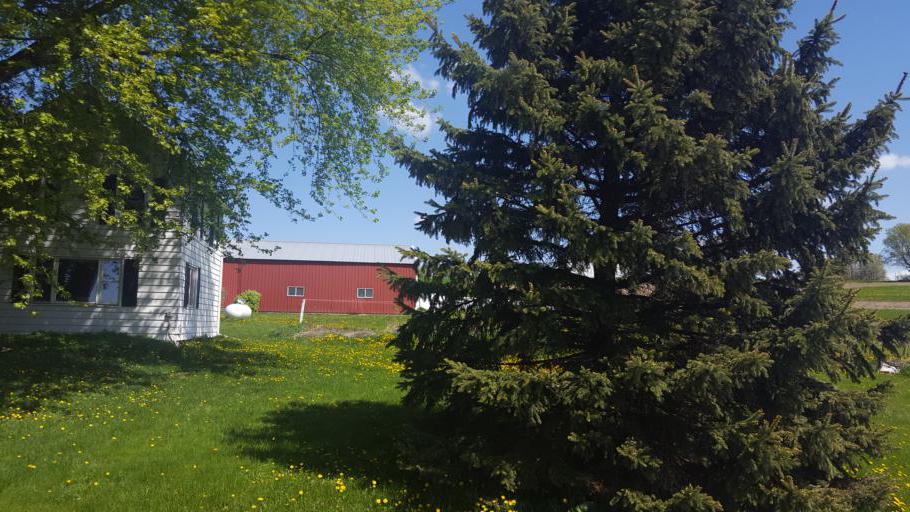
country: US
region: Wisconsin
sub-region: Vernon County
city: Hillsboro
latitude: 43.6335
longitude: -90.3730
